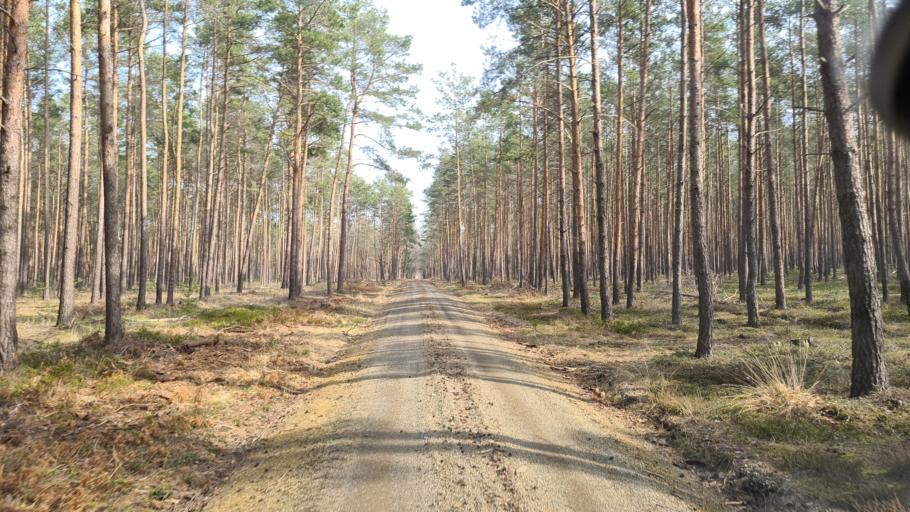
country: DE
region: Brandenburg
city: Trobitz
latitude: 51.6310
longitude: 13.4336
